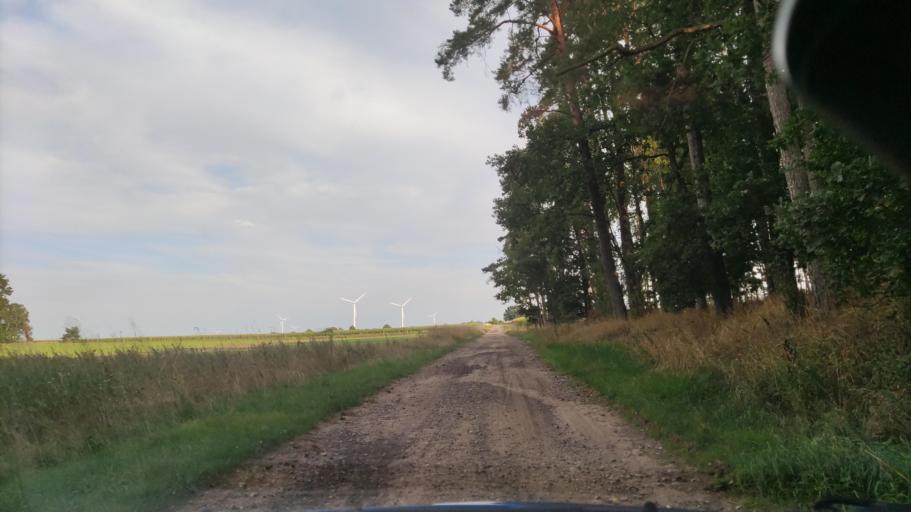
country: DE
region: Lower Saxony
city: Dahlem
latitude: 53.2125
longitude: 10.7389
